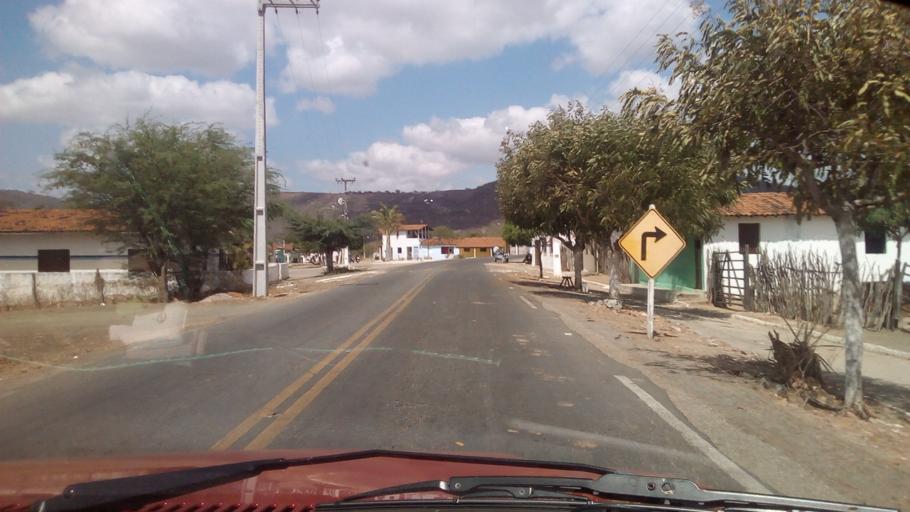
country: BR
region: Paraiba
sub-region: Dona Ines
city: Dona Ines
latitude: -6.5347
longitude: -35.6532
